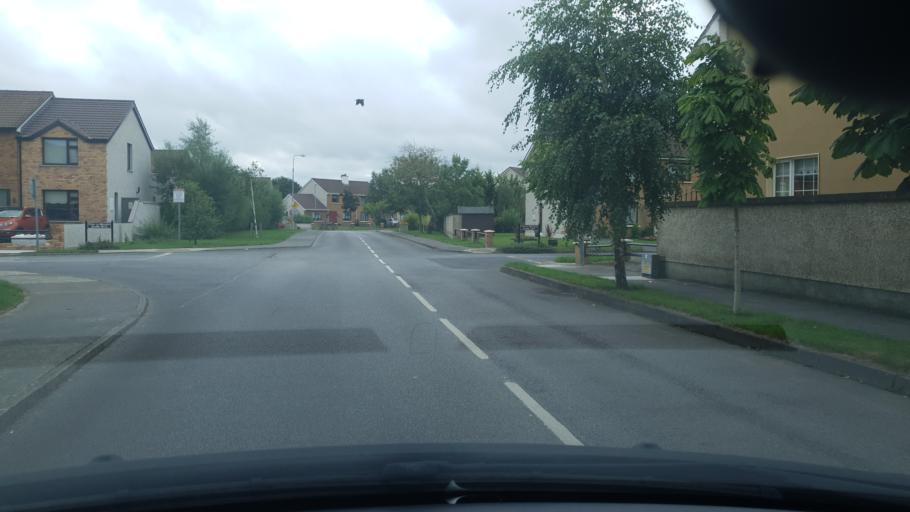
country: IE
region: Munster
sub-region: Ciarrai
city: Tralee
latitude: 52.2587
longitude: -9.6839
